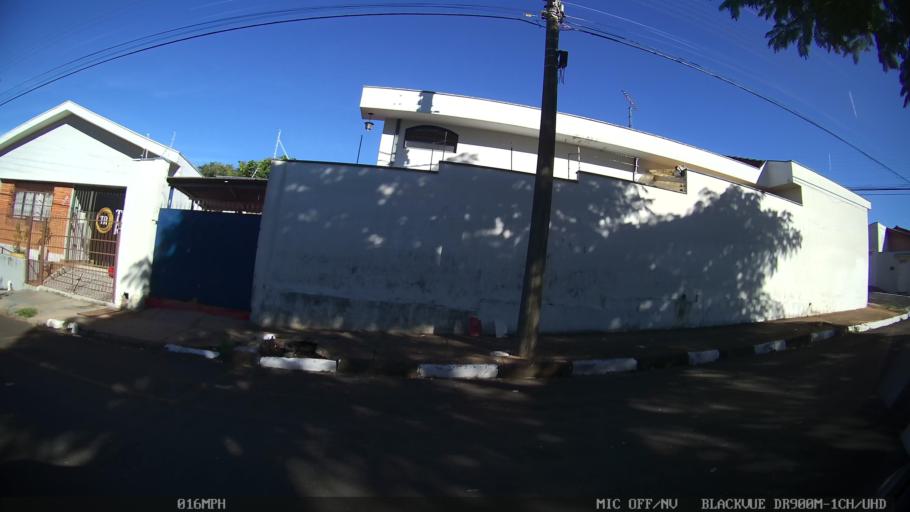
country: BR
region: Sao Paulo
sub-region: Franca
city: Franca
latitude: -20.5470
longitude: -47.4112
